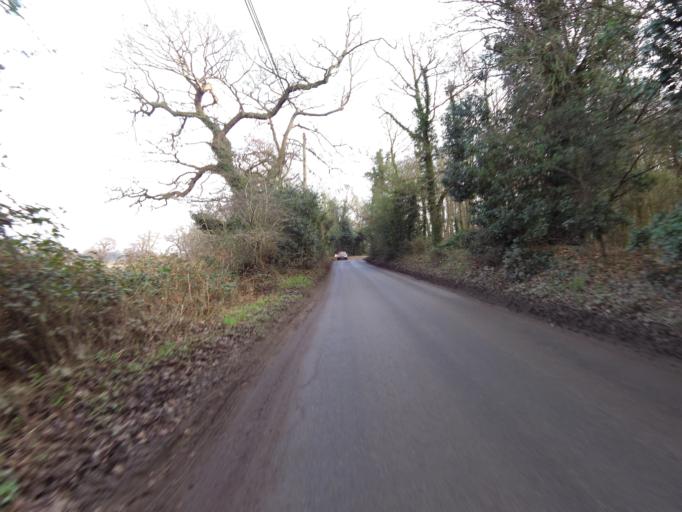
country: GB
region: England
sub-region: Suffolk
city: Woodbridge
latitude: 52.0711
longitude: 1.2927
